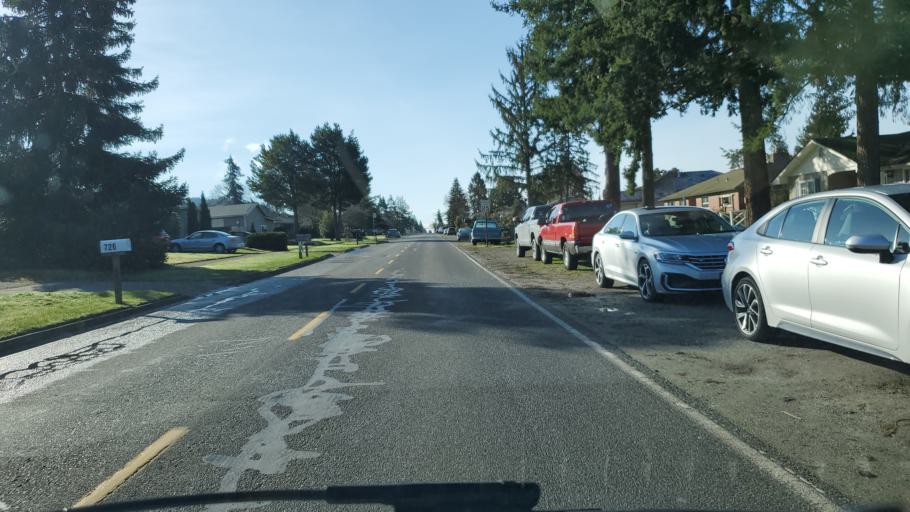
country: US
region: Washington
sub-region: Skagit County
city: Mount Vernon
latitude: 48.4276
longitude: -122.3231
